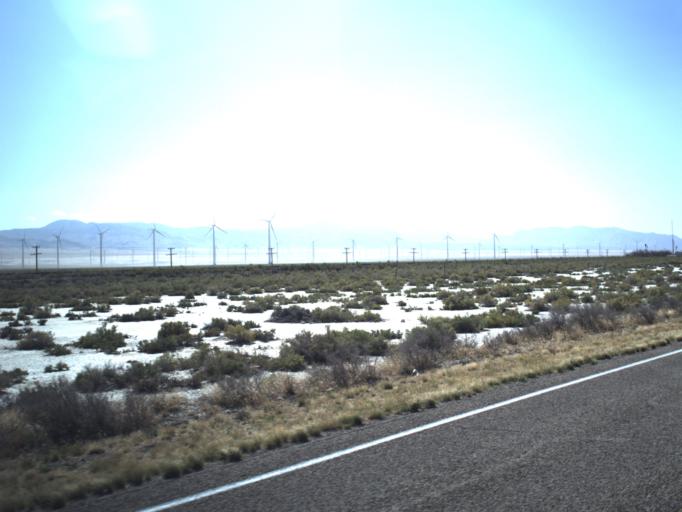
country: US
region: Utah
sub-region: Beaver County
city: Milford
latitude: 38.6054
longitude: -112.9867
